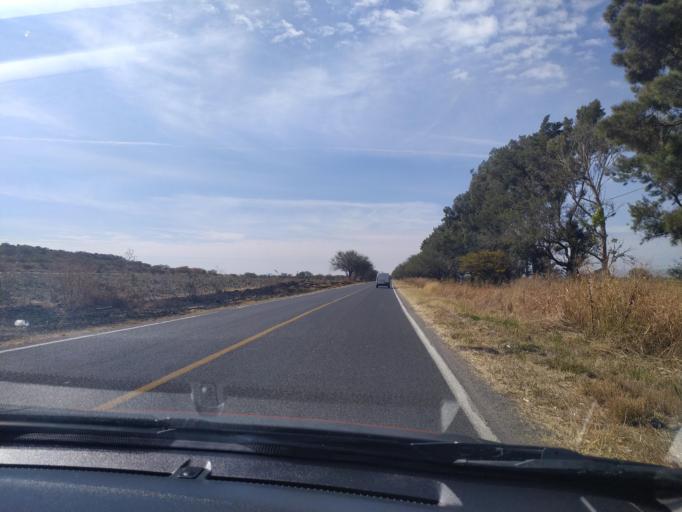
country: MX
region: Guanajuato
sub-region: San Francisco del Rincon
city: San Ignacio de Hidalgo
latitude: 20.9279
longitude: -101.8519
